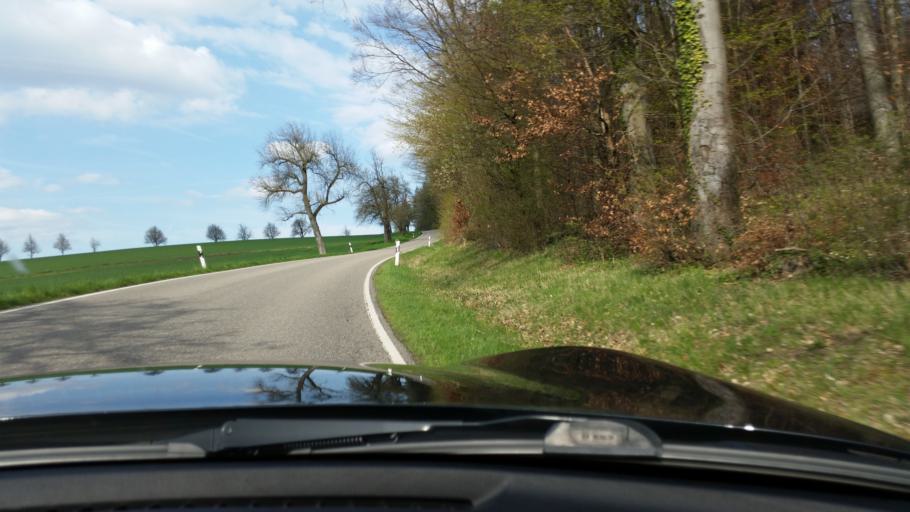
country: DE
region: Baden-Wuerttemberg
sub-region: Regierungsbezirk Stuttgart
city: Neudenau
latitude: 49.2763
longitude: 9.3070
